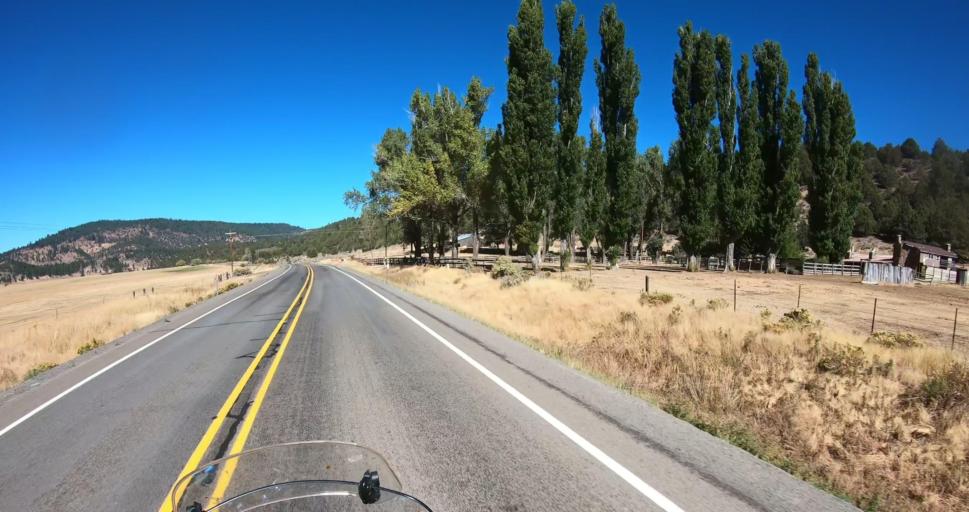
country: US
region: Oregon
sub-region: Lake County
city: Lakeview
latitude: 42.3713
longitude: -120.2974
